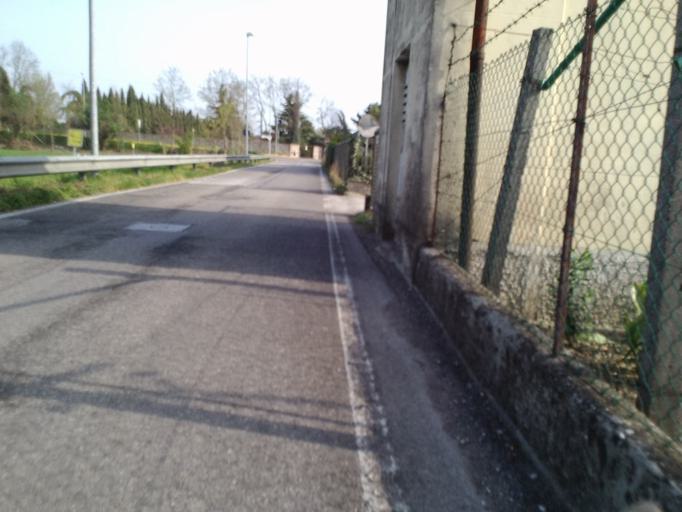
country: IT
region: Veneto
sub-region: Provincia di Verona
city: Dossobuono
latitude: 45.4164
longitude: 10.9445
